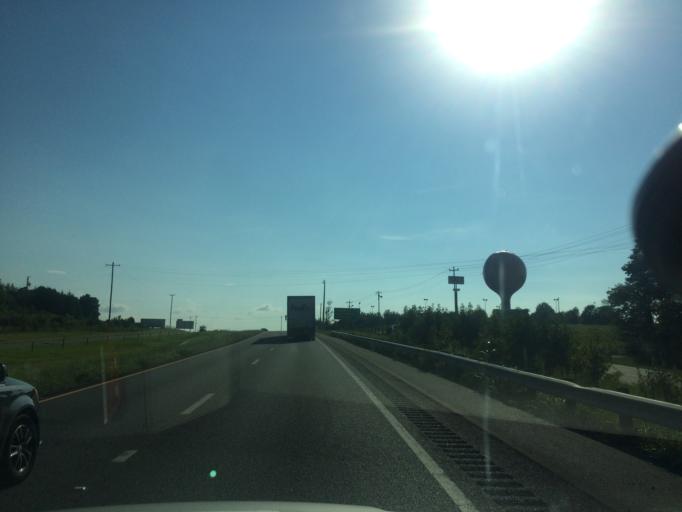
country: US
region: South Carolina
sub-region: Cherokee County
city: Gaffney
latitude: 35.0958
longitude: -81.6824
